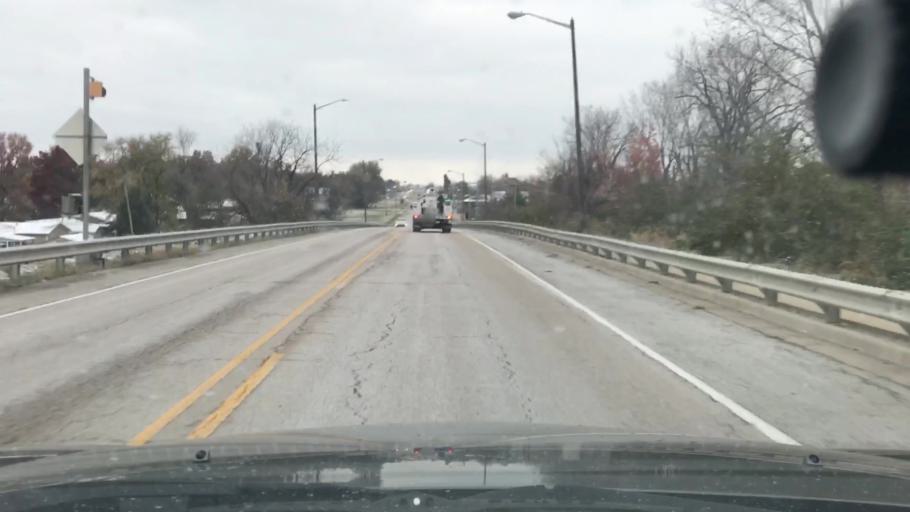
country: US
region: Illinois
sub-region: Madison County
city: Pontoon Beach
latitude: 38.7246
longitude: -90.0707
